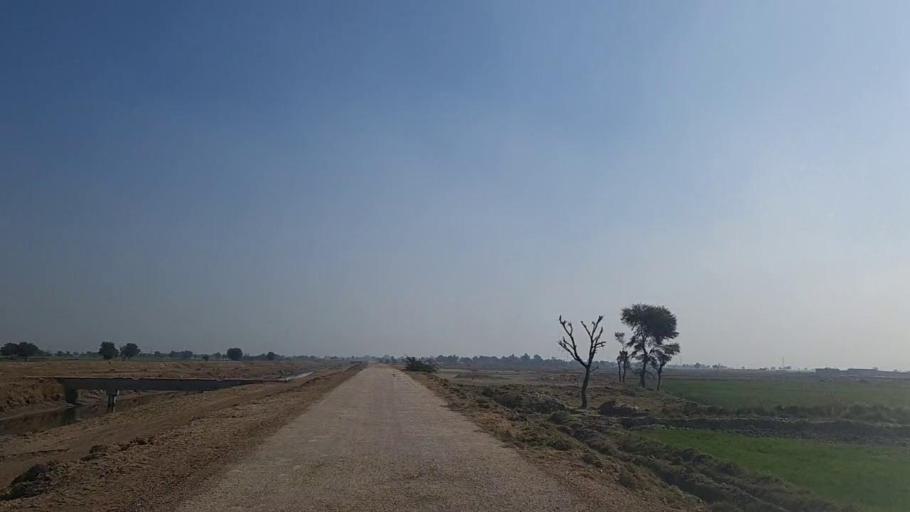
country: PK
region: Sindh
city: Shahpur Chakar
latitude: 26.1878
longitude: 68.5573
